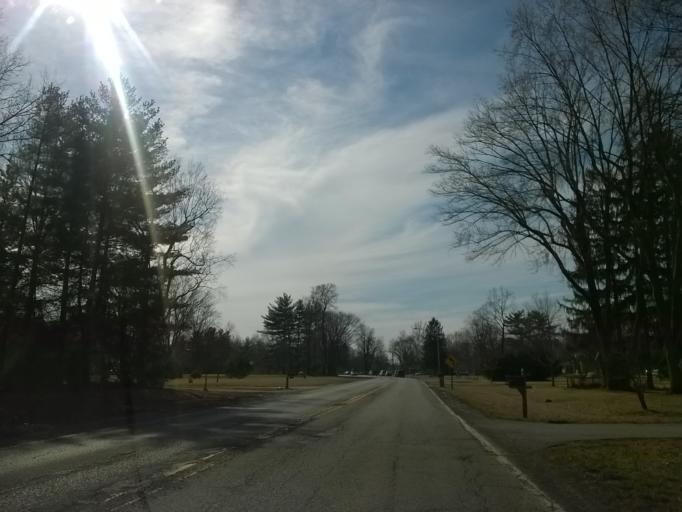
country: US
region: Indiana
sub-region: Marion County
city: Meridian Hills
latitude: 39.8576
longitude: -86.1854
